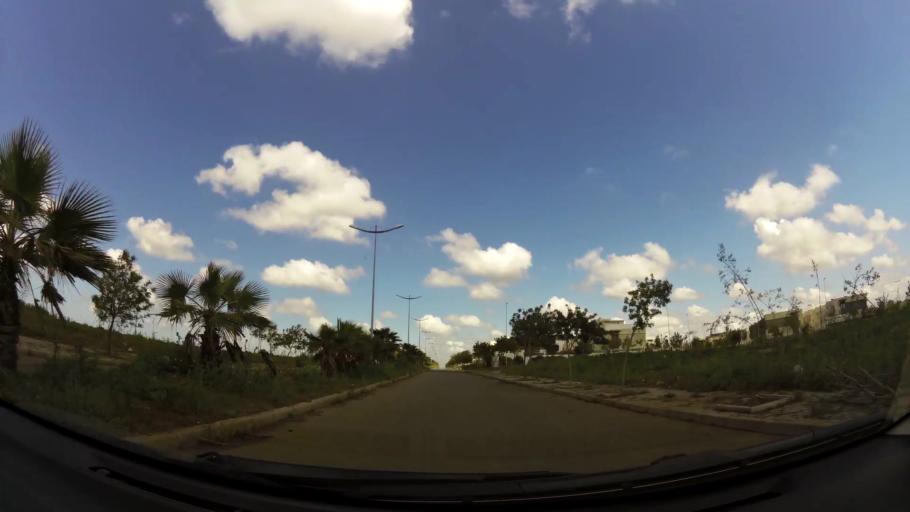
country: MA
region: Grand Casablanca
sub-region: Nouaceur
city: Dar Bouazza
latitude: 33.4231
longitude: -7.8246
